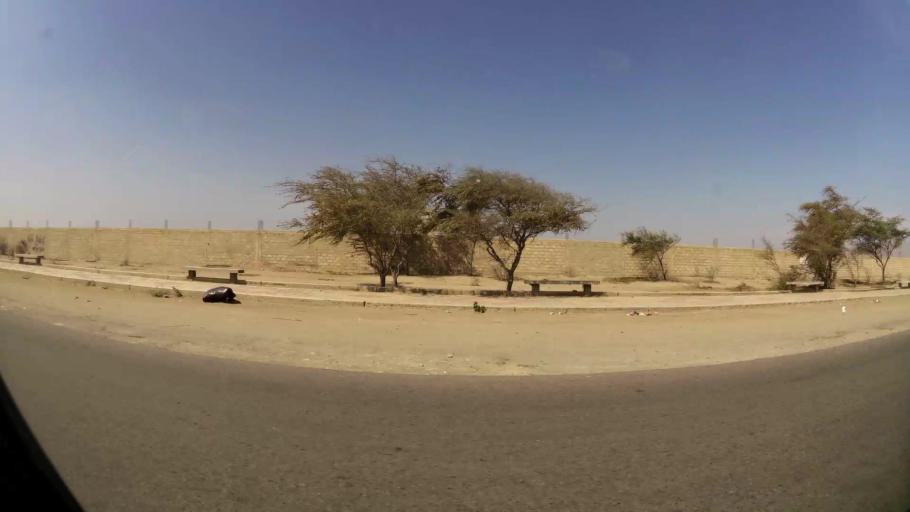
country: PE
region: Lambayeque
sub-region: Provincia de Chiclayo
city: Chiclayo
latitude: -6.7907
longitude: -79.8322
